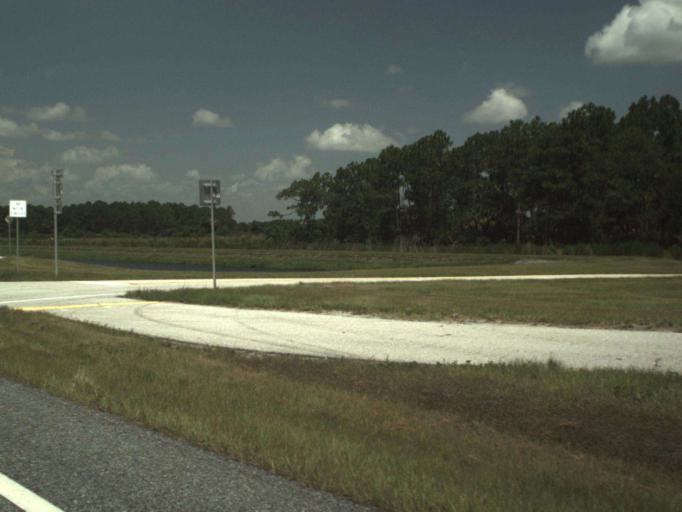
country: US
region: Florida
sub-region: Okeechobee County
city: Taylor Creek
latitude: 27.3654
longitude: -80.6100
